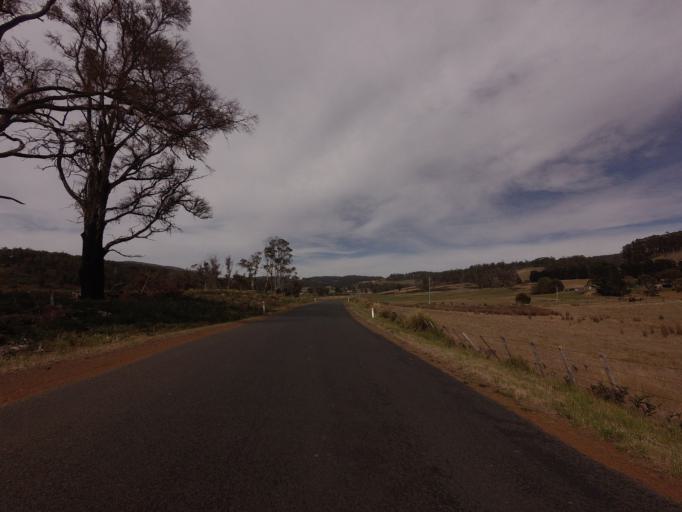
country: AU
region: Tasmania
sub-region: Sorell
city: Sorell
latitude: -42.4559
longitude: 147.5744
